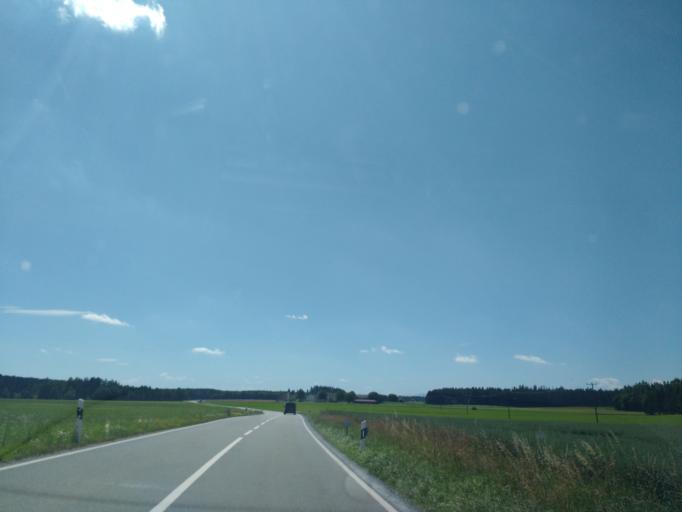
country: DE
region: Bavaria
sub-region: Upper Bavaria
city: Kienberg
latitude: 48.0645
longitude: 12.4235
